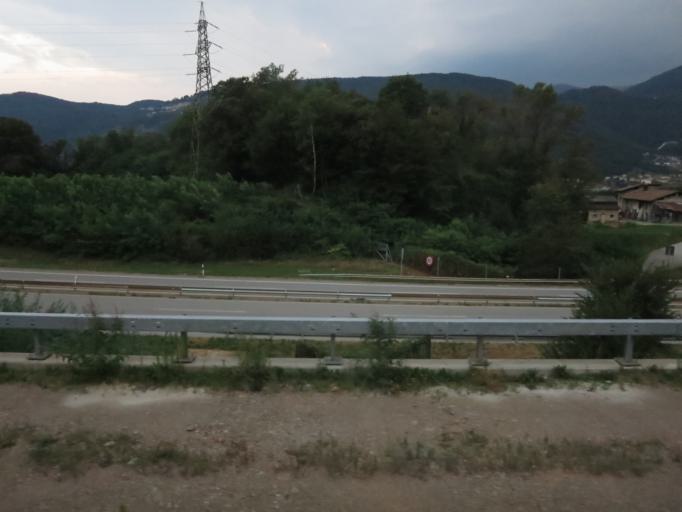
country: CH
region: Ticino
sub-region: Lugano District
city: Massagno
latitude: 46.0227
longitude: 8.9342
